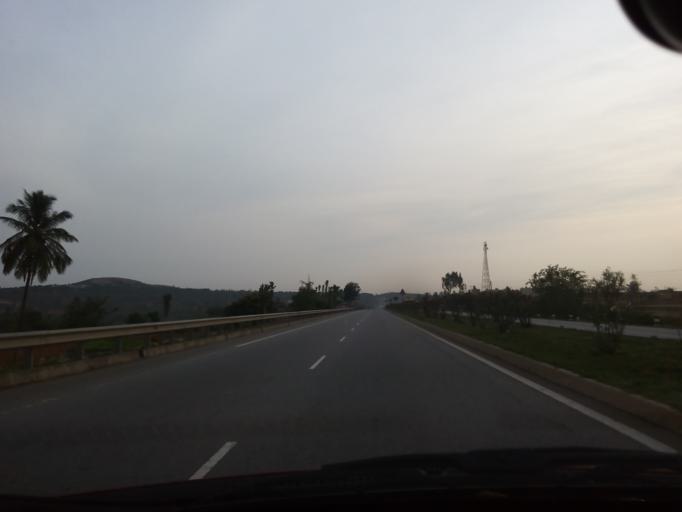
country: IN
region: Karnataka
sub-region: Chikkaballapur
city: Chik Ballapur
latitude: 13.5375
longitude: 77.7683
